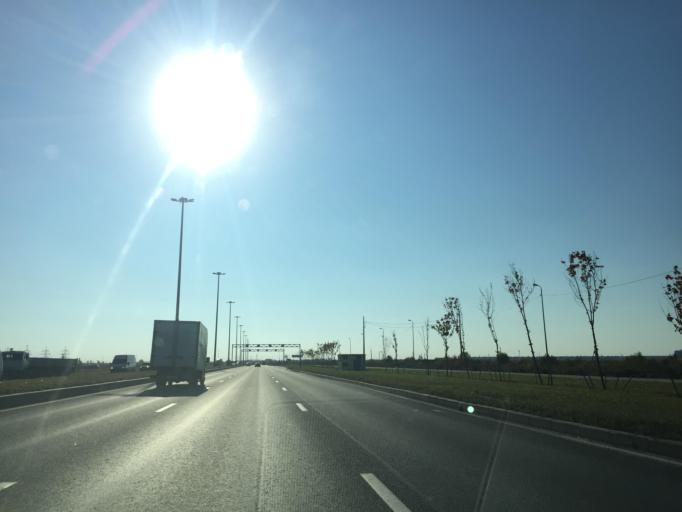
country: RU
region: St.-Petersburg
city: Petro-Slavyanka
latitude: 59.7741
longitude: 30.4991
